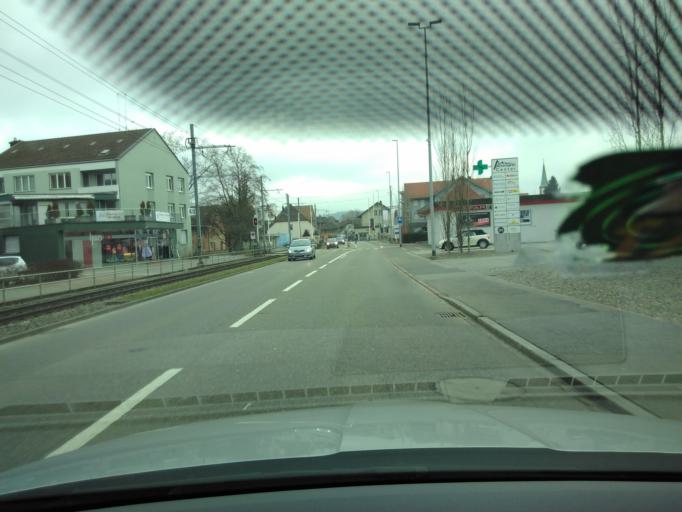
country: CH
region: Aargau
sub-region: Bezirk Aarau
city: Oberentfelden
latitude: 47.3540
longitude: 8.0472
